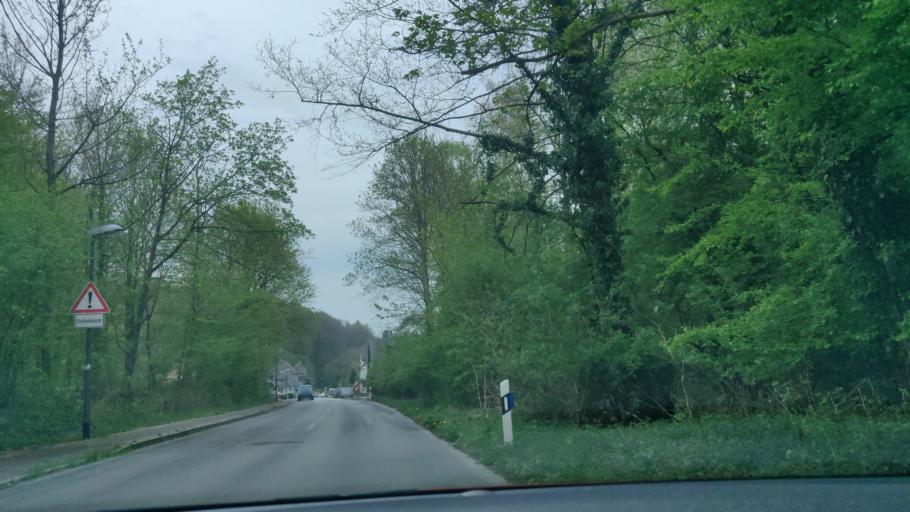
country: DE
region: North Rhine-Westphalia
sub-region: Regierungsbezirk Dusseldorf
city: Velbert
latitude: 51.3848
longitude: 7.0406
